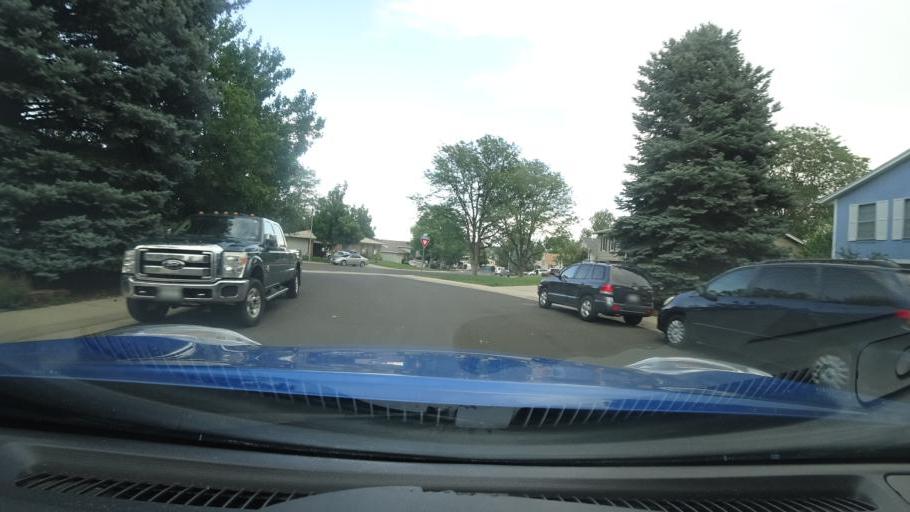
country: US
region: Colorado
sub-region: Adams County
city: Aurora
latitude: 39.6879
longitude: -104.8087
